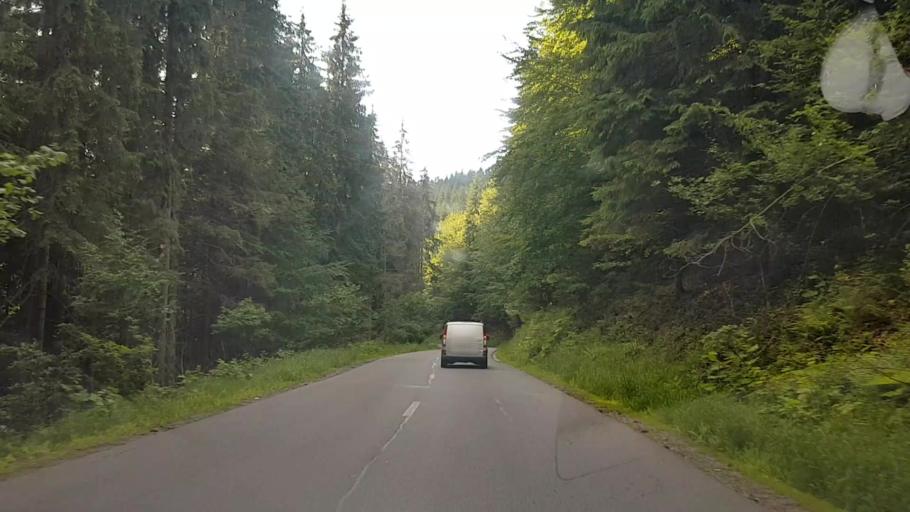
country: RO
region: Harghita
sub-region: Comuna Varsag
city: Varsag
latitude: 46.6710
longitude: 25.3290
